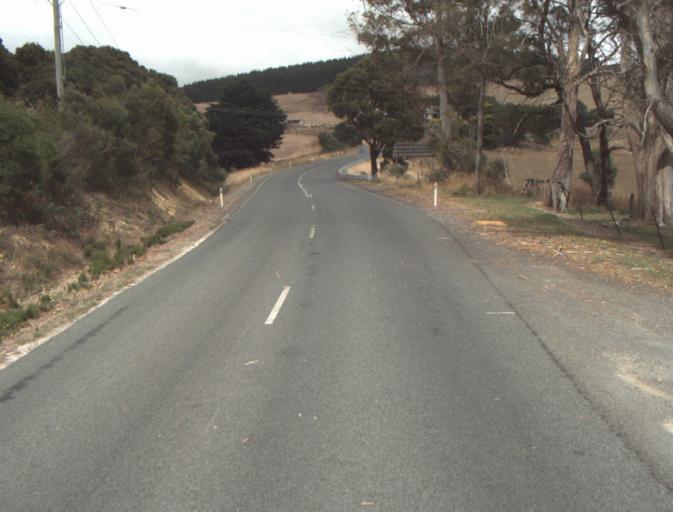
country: AU
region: Tasmania
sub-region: Dorset
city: Bridport
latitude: -41.1634
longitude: 147.2407
